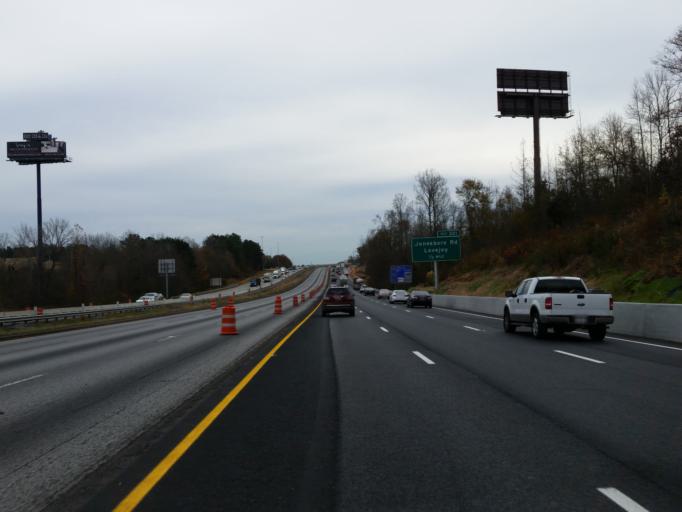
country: US
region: Georgia
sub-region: Henry County
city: McDonough
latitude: 33.4718
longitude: -84.2142
